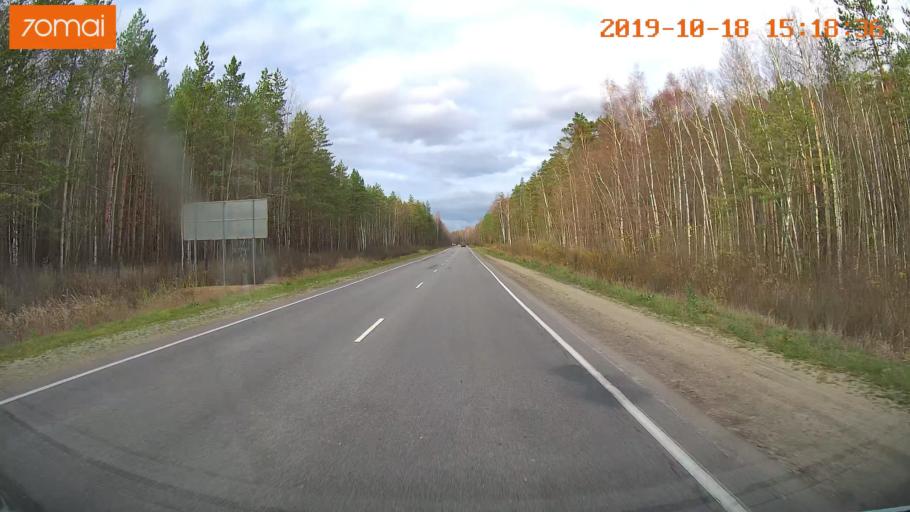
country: RU
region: Vladimir
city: Anopino
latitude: 55.6614
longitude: 40.7303
